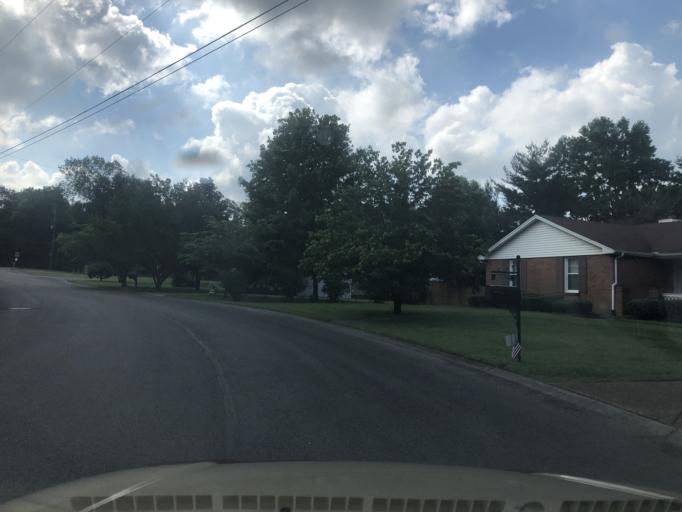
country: US
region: Tennessee
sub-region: Wilson County
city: Green Hill
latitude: 36.2307
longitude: -86.5927
